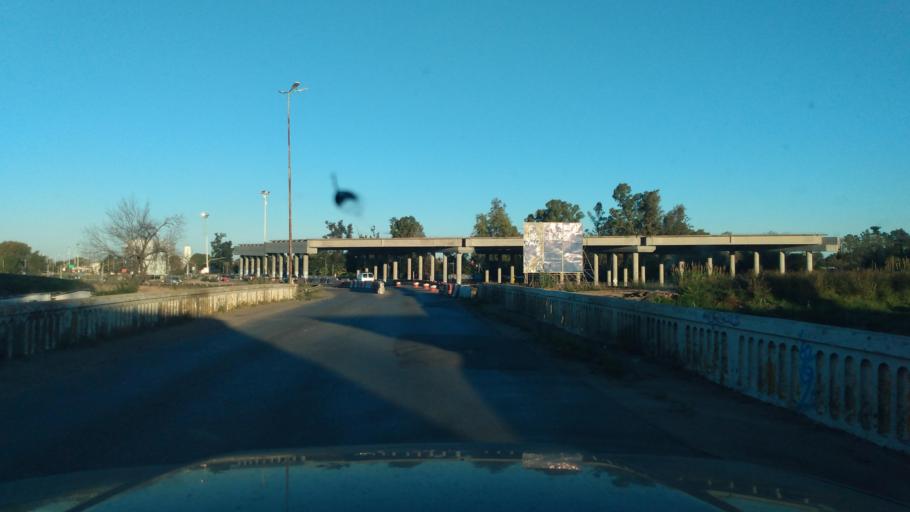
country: AR
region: Buenos Aires
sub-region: Partido de Merlo
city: Merlo
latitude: -34.6592
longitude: -58.7560
